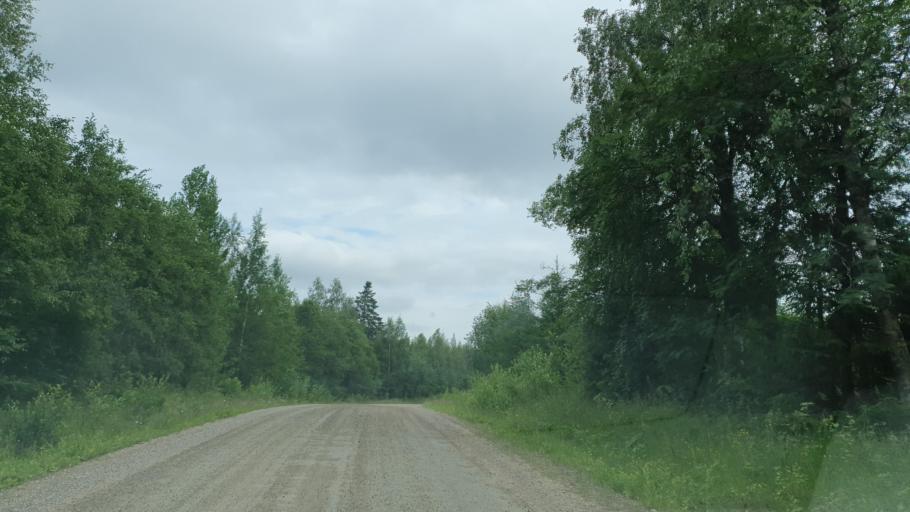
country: FI
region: Kainuu
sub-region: Kehys-Kainuu
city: Kuhmo
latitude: 63.9336
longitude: 29.4545
